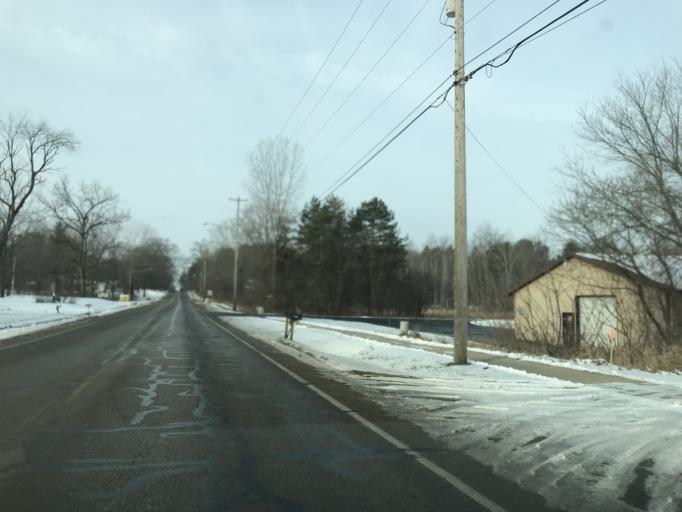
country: US
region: Michigan
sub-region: Kent County
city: Byron Center
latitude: 42.7252
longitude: -85.7330
